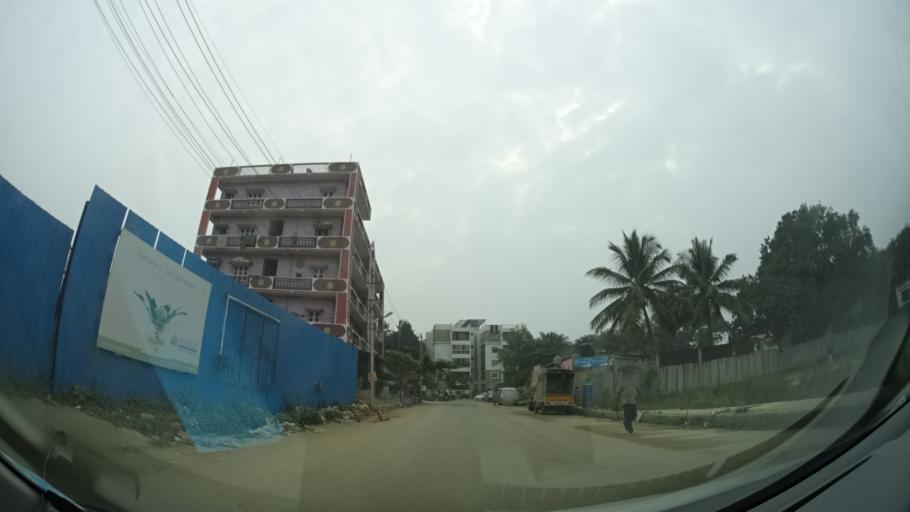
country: IN
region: Karnataka
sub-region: Bangalore Rural
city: Hoskote
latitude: 12.9772
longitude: 77.7391
